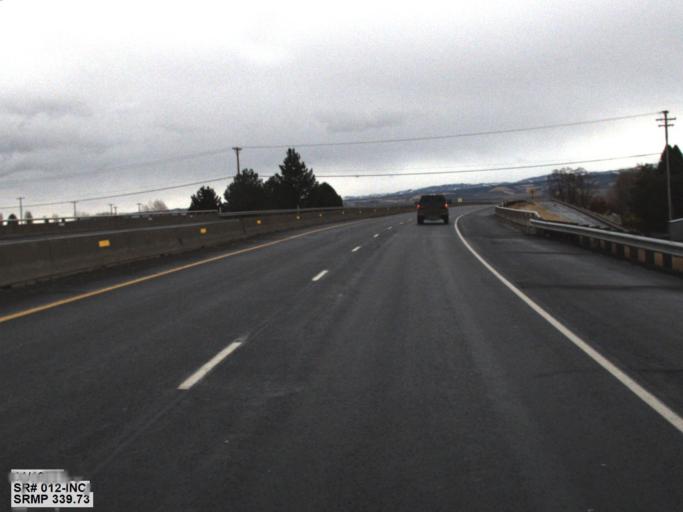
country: US
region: Washington
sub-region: Walla Walla County
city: Walla Walla East
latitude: 46.0838
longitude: -118.2843
